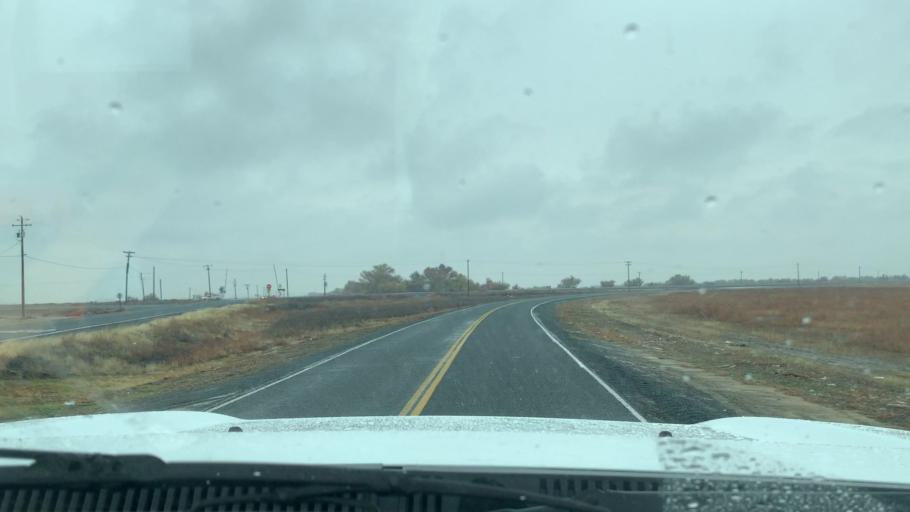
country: US
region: California
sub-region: Tulare County
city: Alpaugh
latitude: 35.8915
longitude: -119.4030
